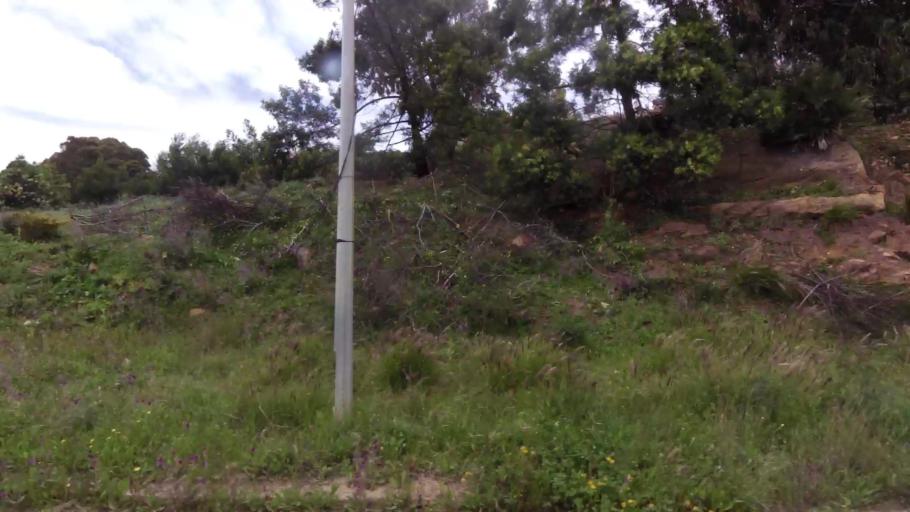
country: MA
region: Tanger-Tetouan
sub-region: Tanger-Assilah
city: Tangier
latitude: 35.7802
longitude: -5.8568
